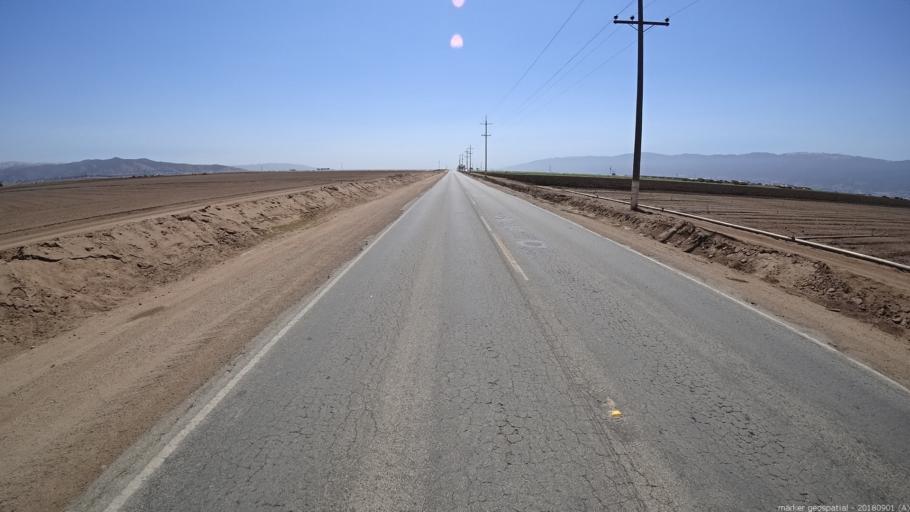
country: US
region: California
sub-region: Monterey County
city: Chualar
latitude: 36.5943
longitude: -121.5055
